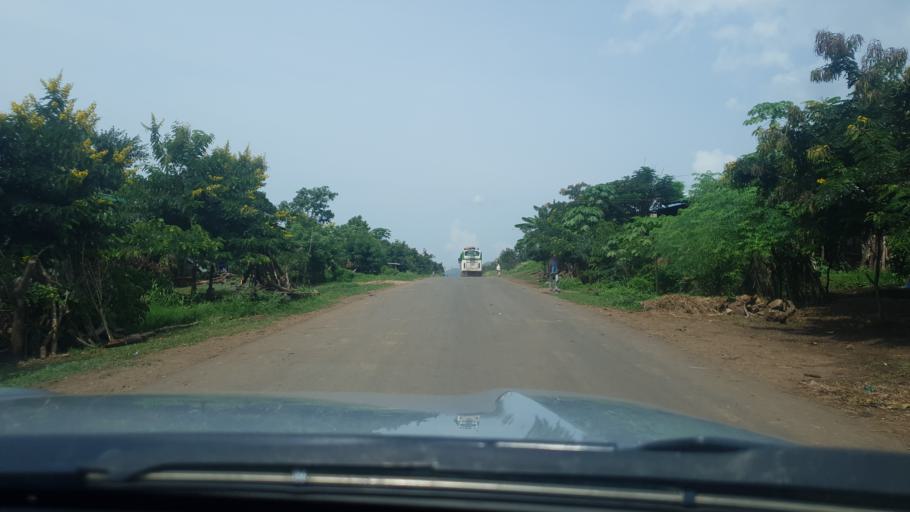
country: ET
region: Southern Nations, Nationalities, and People's Region
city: Mizan Teferi
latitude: 6.6959
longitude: 35.1861
